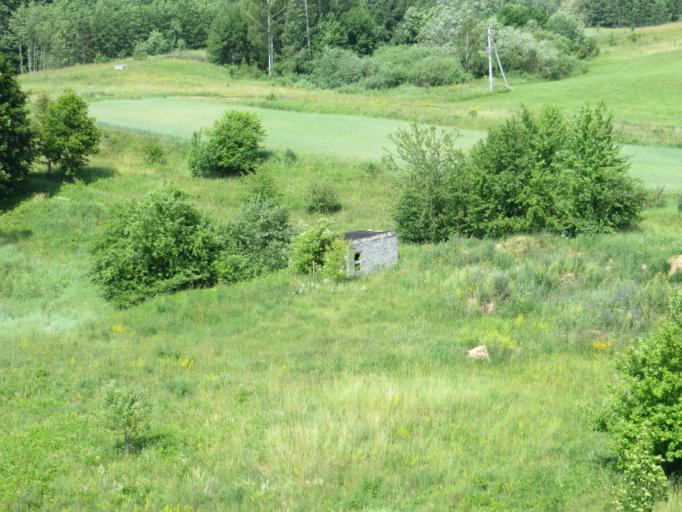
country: LT
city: Lazdijai
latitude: 54.2279
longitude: 23.3907
